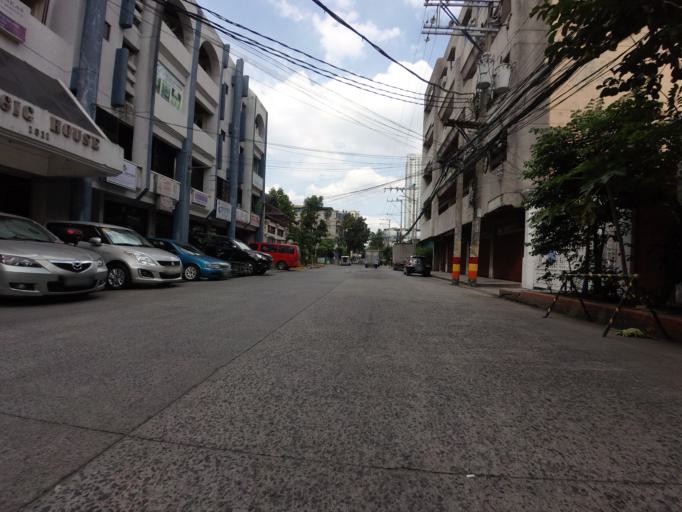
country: PH
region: Metro Manila
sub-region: City of Manila
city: Port Area
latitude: 14.5722
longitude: 120.9877
